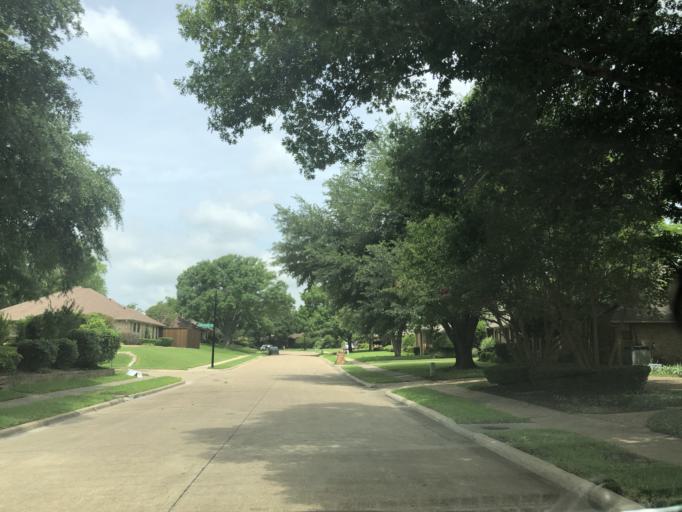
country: US
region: Texas
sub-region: Dallas County
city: Garland
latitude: 32.8529
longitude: -96.6195
